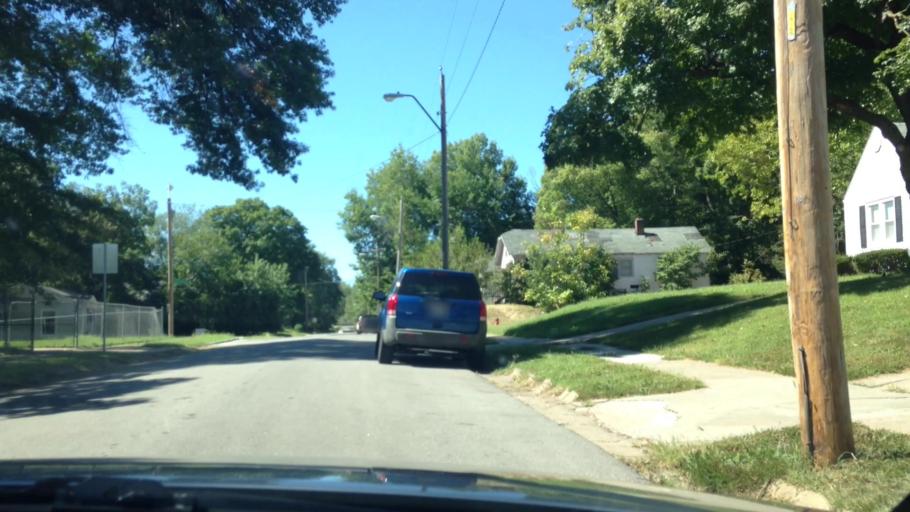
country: US
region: Kansas
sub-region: Johnson County
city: Mission Hills
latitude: 39.0031
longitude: -94.5479
